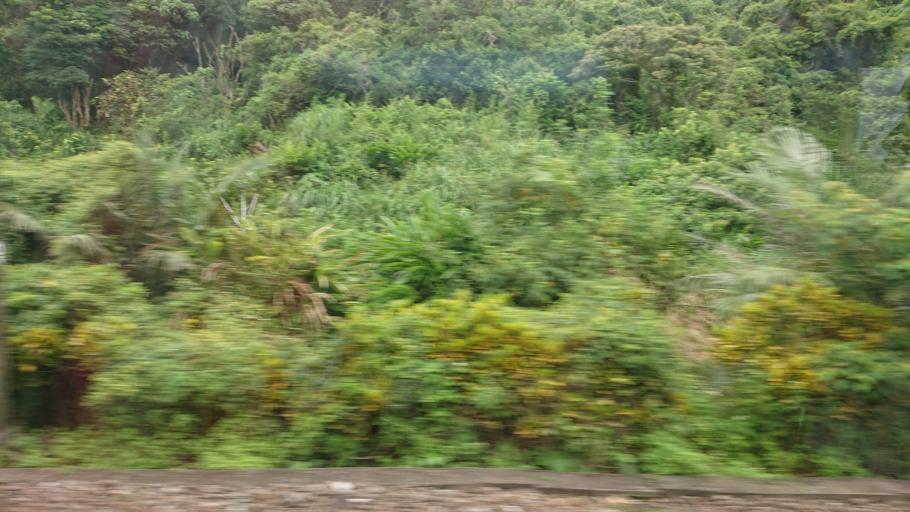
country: TW
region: Taiwan
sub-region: Keelung
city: Keelung
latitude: 24.9596
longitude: 121.9184
